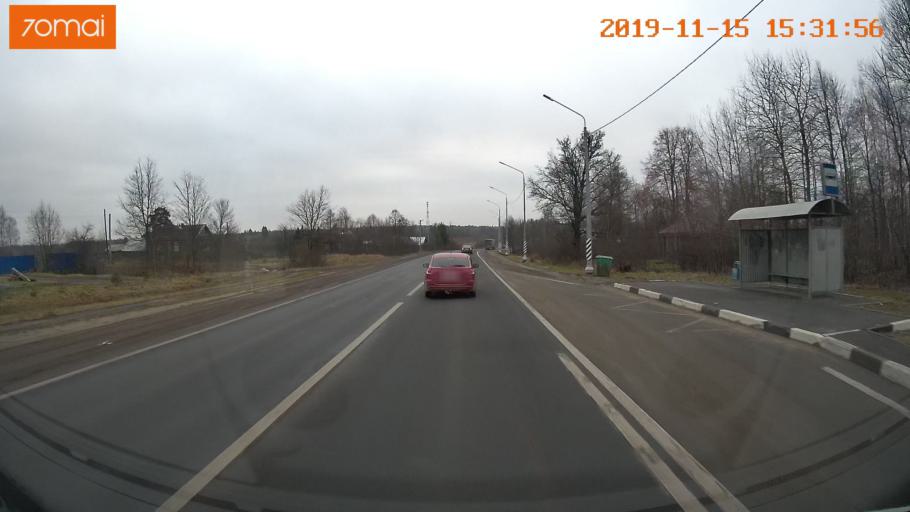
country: RU
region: Jaroslavl
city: Danilov
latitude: 58.0951
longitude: 40.1042
